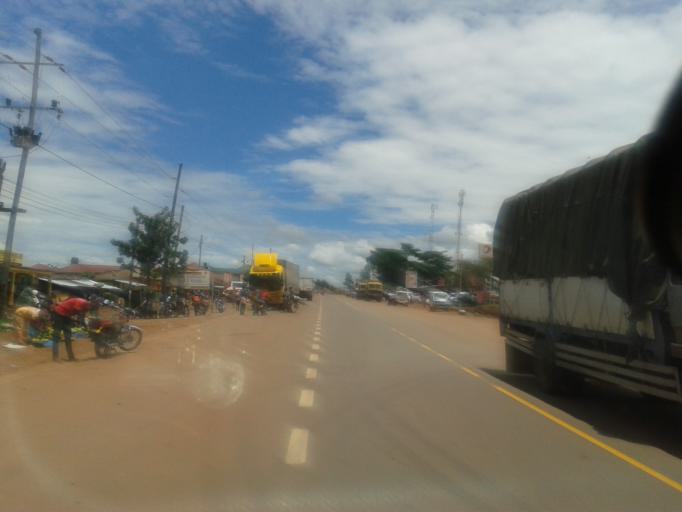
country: UG
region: Western Region
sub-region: Kiryandongo District
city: Kiryandongo
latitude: 1.8098
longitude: 32.0117
